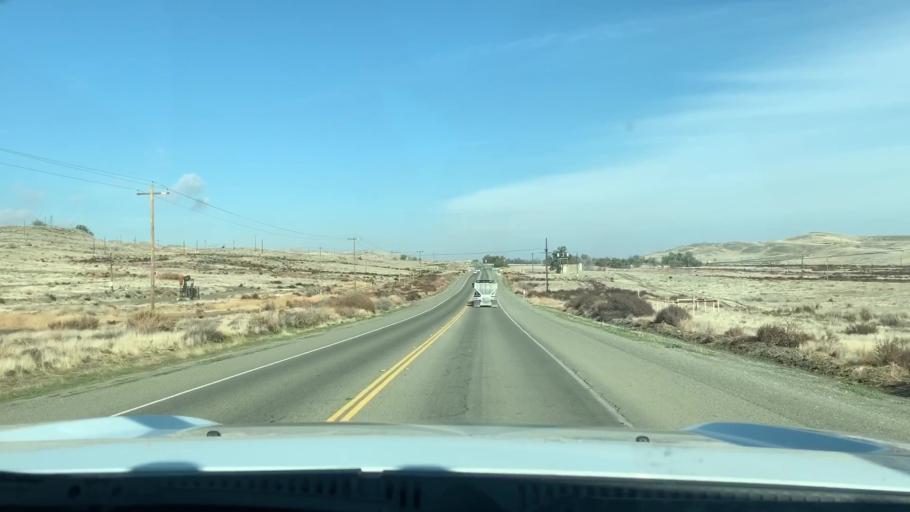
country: US
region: California
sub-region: Fresno County
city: Coalinga
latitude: 36.2403
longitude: -120.3147
